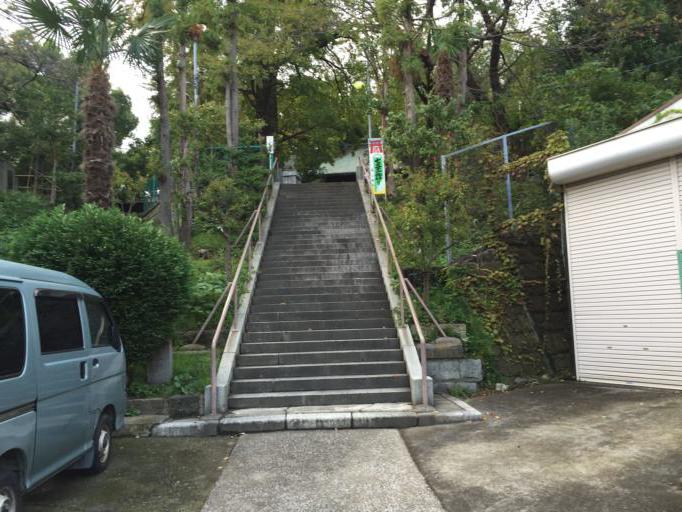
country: JP
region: Kanagawa
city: Yokohama
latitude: 35.4283
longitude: 139.6149
